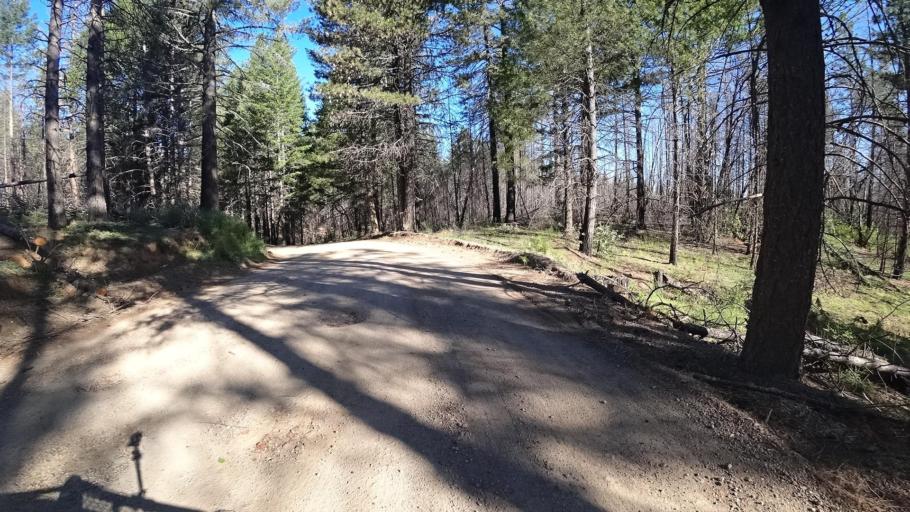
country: US
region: California
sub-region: Lake County
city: Upper Lake
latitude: 39.3513
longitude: -122.9752
